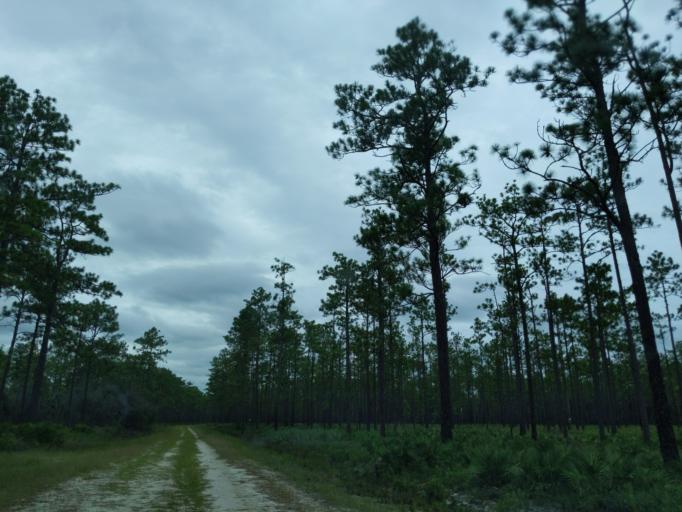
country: US
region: Florida
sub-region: Gadsden County
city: Midway
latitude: 30.3742
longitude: -84.4748
